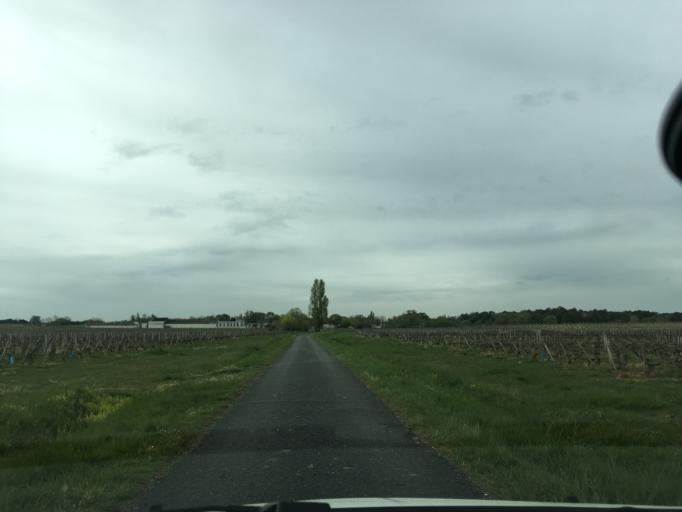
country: FR
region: Aquitaine
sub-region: Departement de la Gironde
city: Lesparre-Medoc
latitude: 45.3189
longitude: -0.8951
